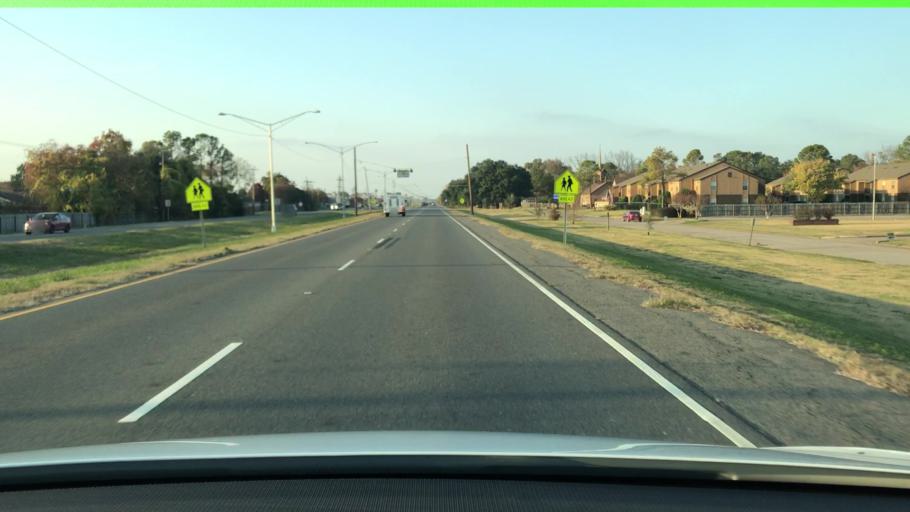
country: US
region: Louisiana
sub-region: Bossier Parish
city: Bossier City
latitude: 32.4152
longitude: -93.7021
